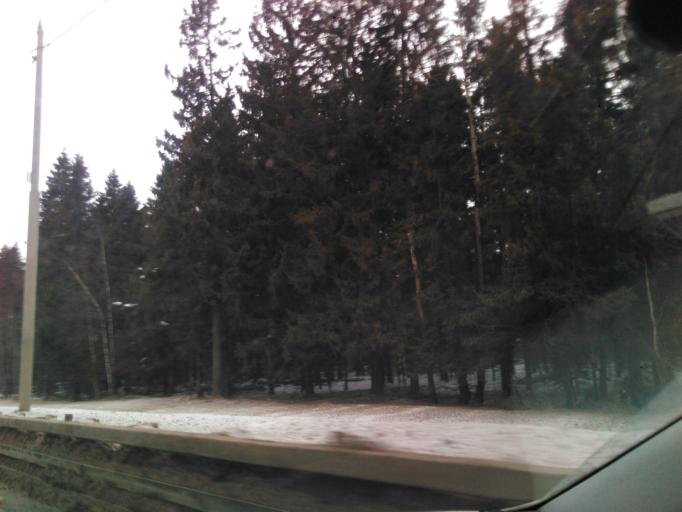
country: RU
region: Moskovskaya
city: Yermolino
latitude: 56.1384
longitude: 37.4849
